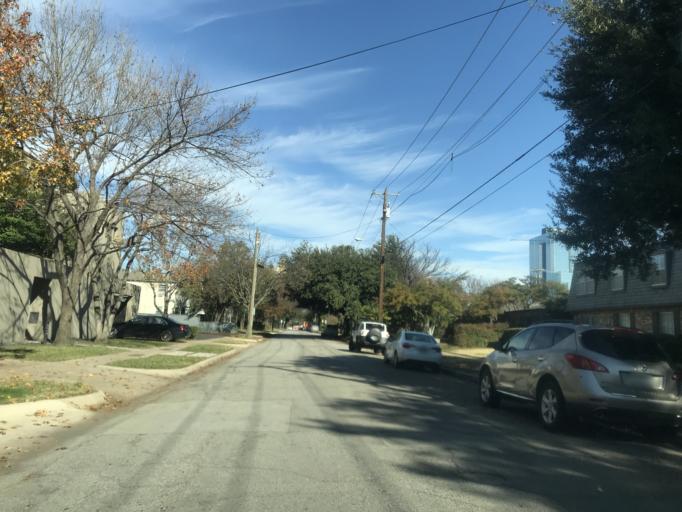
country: US
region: Texas
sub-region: Dallas County
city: Highland Park
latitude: 32.8195
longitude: -96.7925
